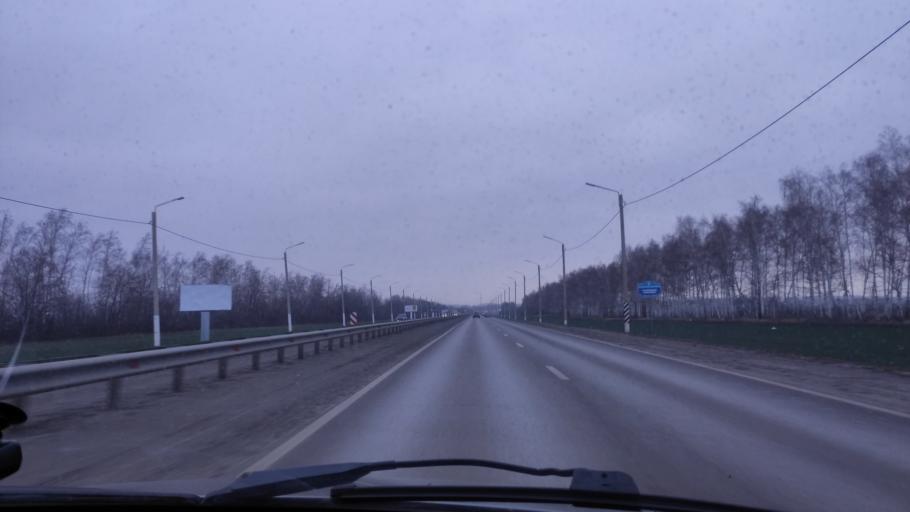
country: RU
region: Tambov
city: Pokrovo-Prigorodnoye
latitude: 52.7250
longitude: 41.3527
